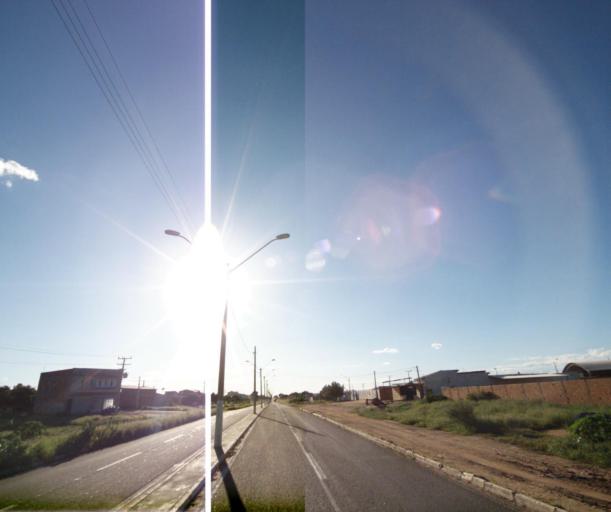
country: BR
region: Bahia
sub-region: Guanambi
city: Guanambi
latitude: -14.2096
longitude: -42.7757
